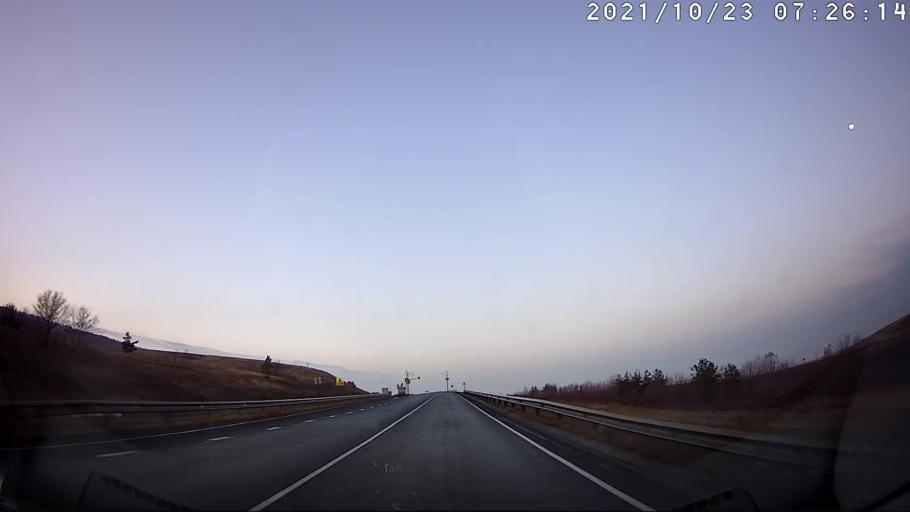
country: RU
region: Saratov
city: Alekseyevka
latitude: 52.3501
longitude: 47.9400
